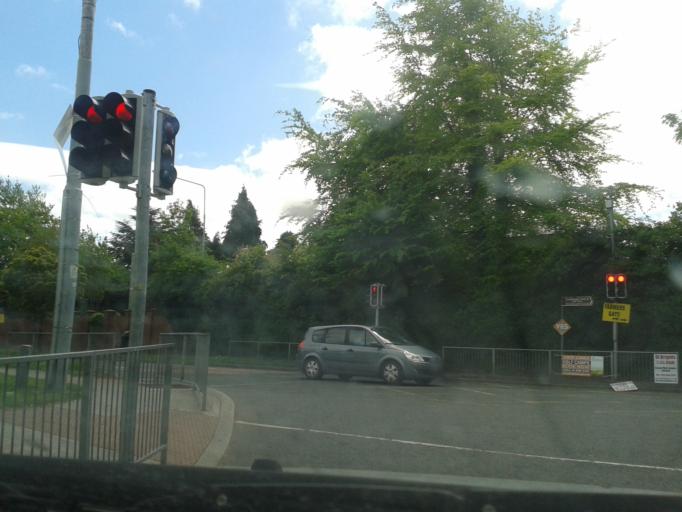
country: IE
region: Leinster
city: Castleknock
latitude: 53.3720
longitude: -6.3584
